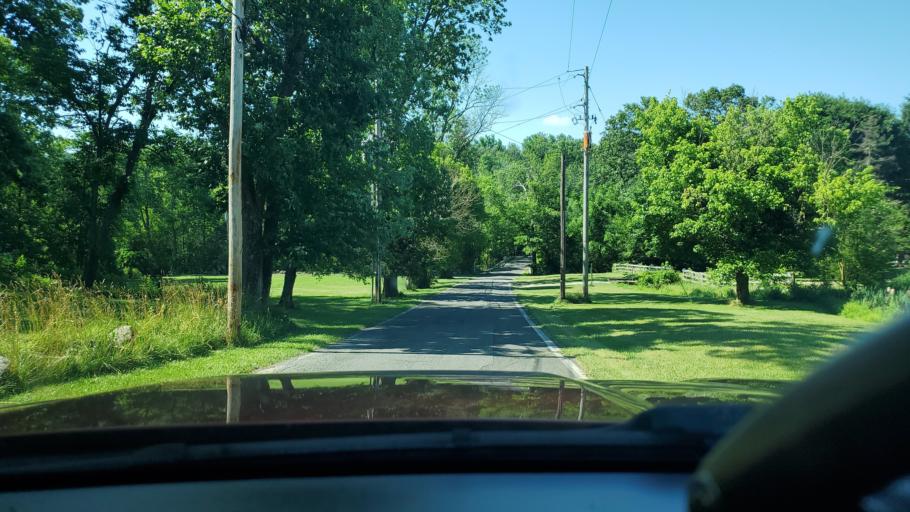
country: US
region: Pennsylvania
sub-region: Montgomery County
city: Red Hill
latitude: 40.3401
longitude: -75.5152
